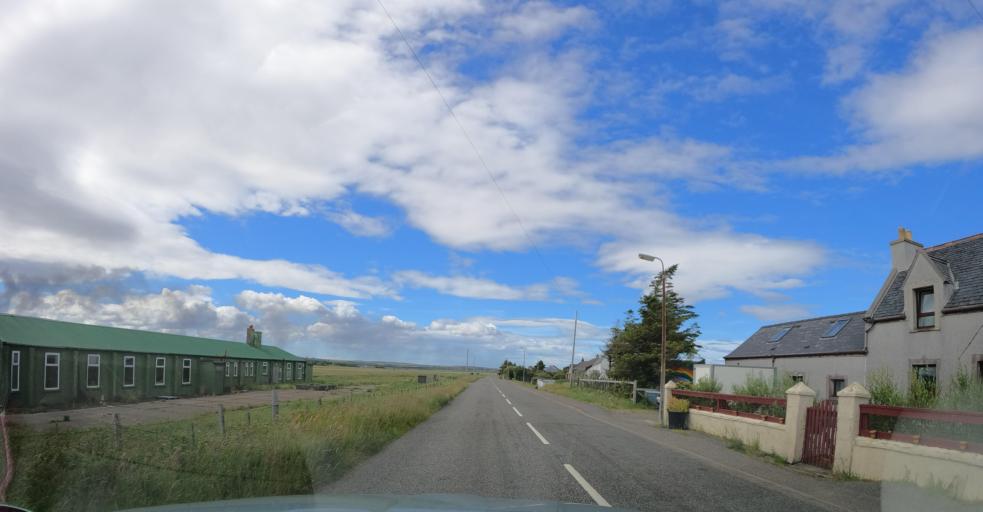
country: GB
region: Scotland
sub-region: Eilean Siar
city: Stornoway
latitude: 58.2062
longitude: -6.3210
